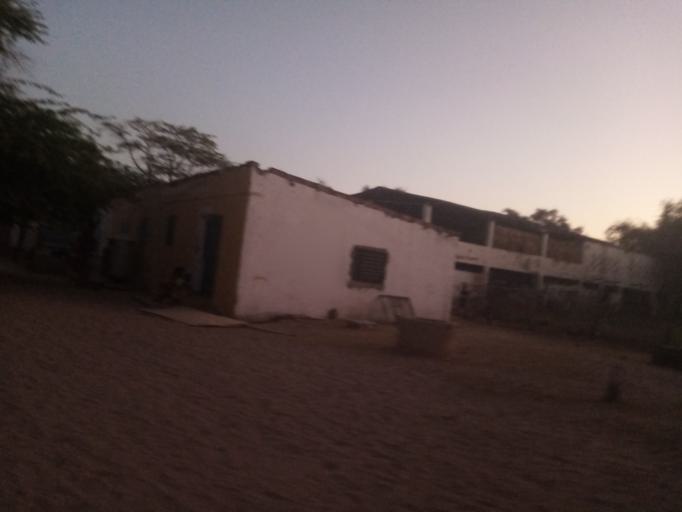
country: SN
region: Saint-Louis
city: Saint-Louis
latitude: 15.9711
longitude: -16.3705
